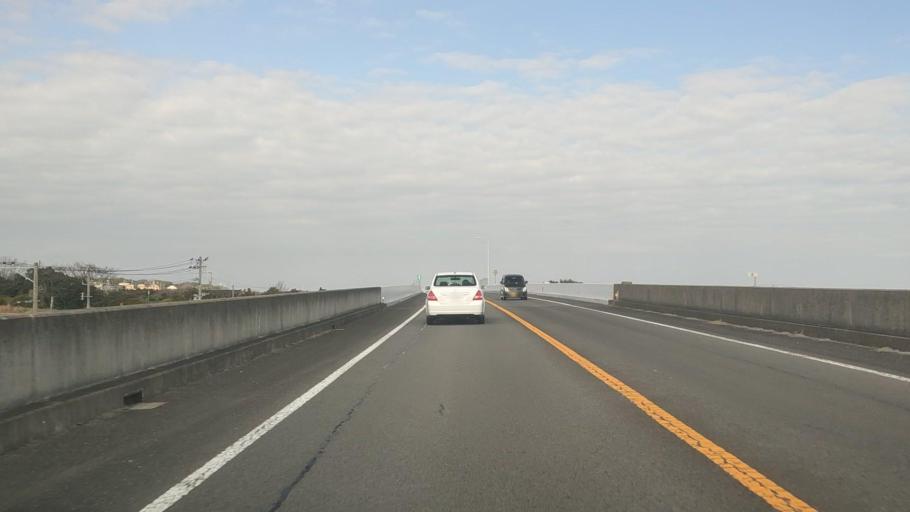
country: JP
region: Nagasaki
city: Shimabara
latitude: 32.7385
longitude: 130.3710
